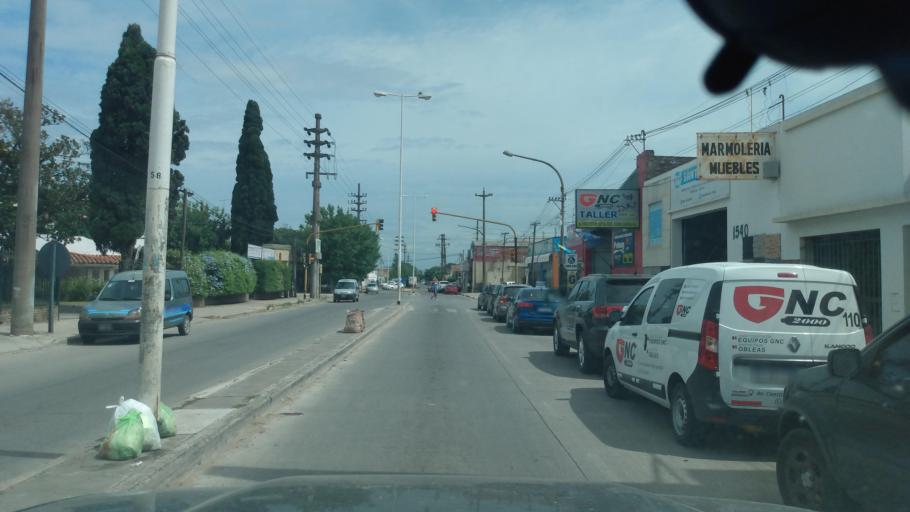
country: AR
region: Buenos Aires
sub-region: Partido de Lujan
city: Lujan
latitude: -34.5661
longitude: -59.0968
